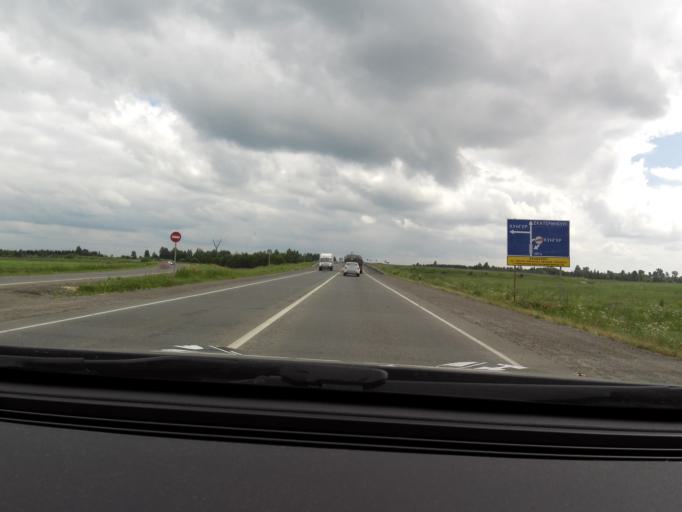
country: RU
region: Perm
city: Kungur
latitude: 57.4062
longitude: 56.8833
